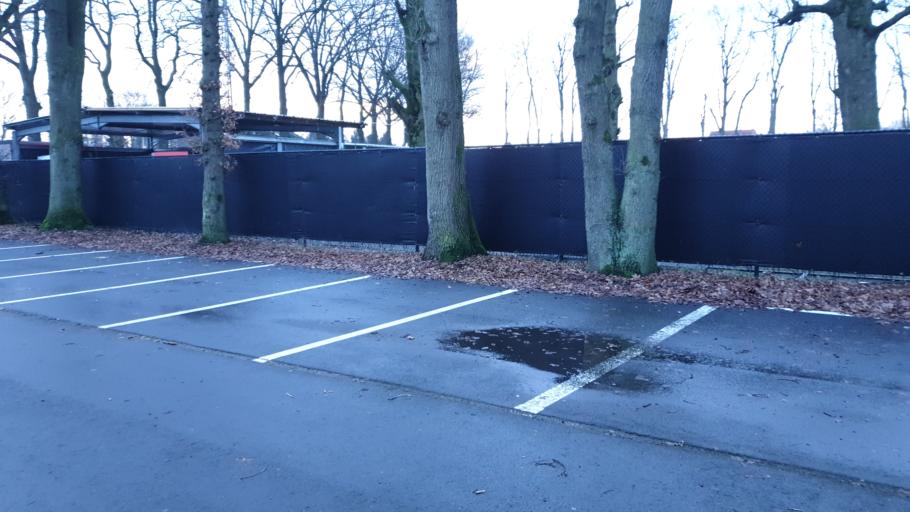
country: BE
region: Flanders
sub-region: Provincie Antwerpen
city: Essen
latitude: 51.4541
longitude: 4.4640
